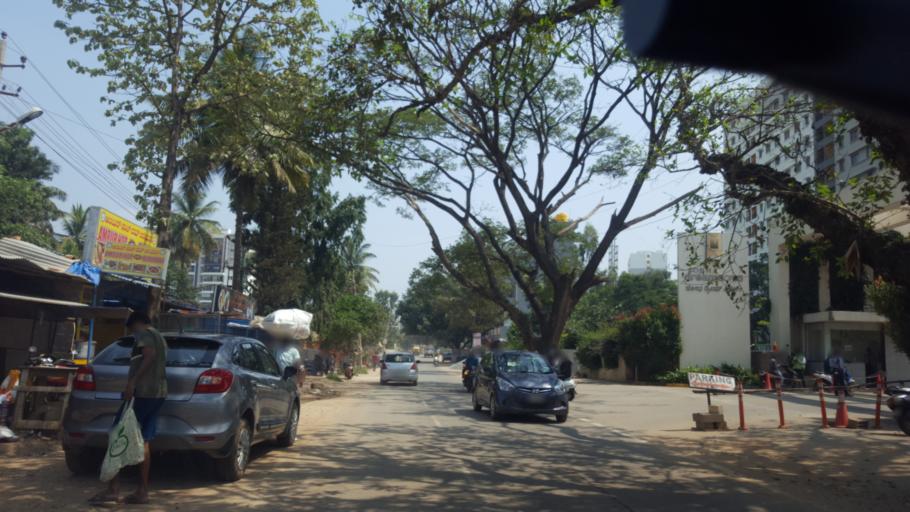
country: IN
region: Karnataka
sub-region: Bangalore Urban
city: Bangalore
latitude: 12.9392
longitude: 77.7199
